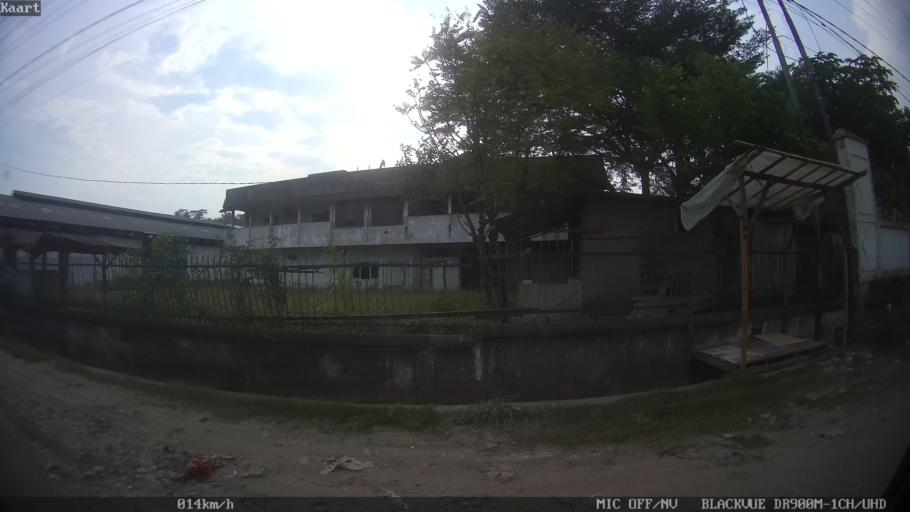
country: ID
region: Lampung
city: Panjang
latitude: -5.4473
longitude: 105.3100
